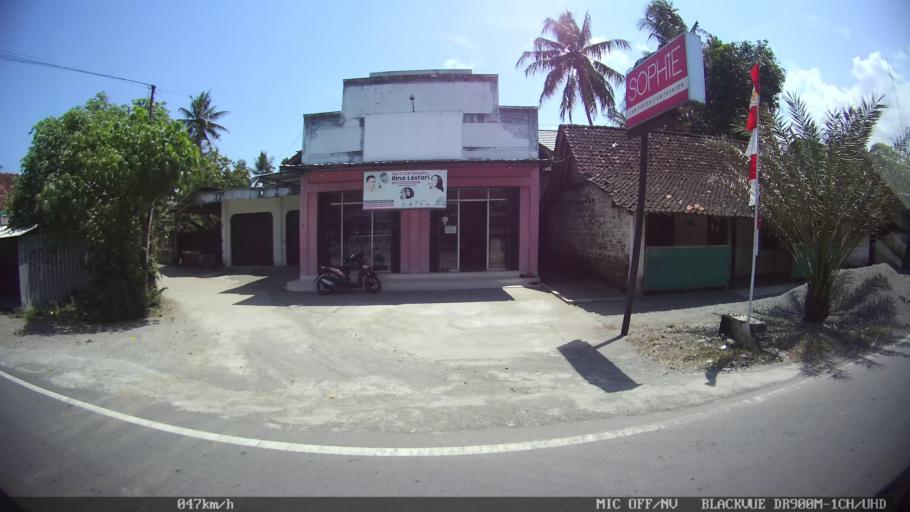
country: ID
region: Daerah Istimewa Yogyakarta
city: Srandakan
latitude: -7.9341
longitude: 110.2621
